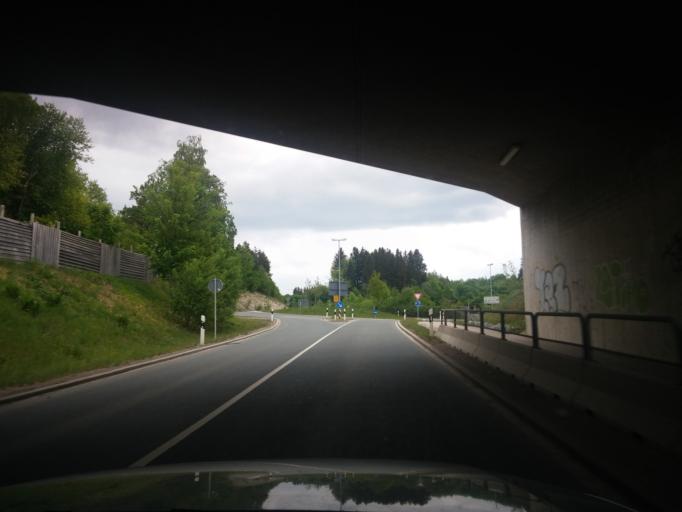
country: DE
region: Bavaria
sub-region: Upper Bavaria
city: Holzkirchen
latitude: 47.8870
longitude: 11.7143
